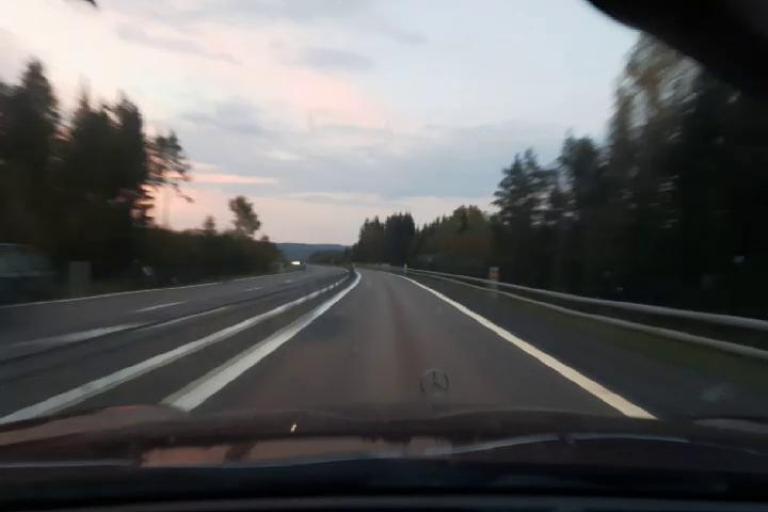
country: SE
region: Vaesternorrland
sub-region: Kramfors Kommun
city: Nordingra
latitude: 62.8870
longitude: 18.0870
